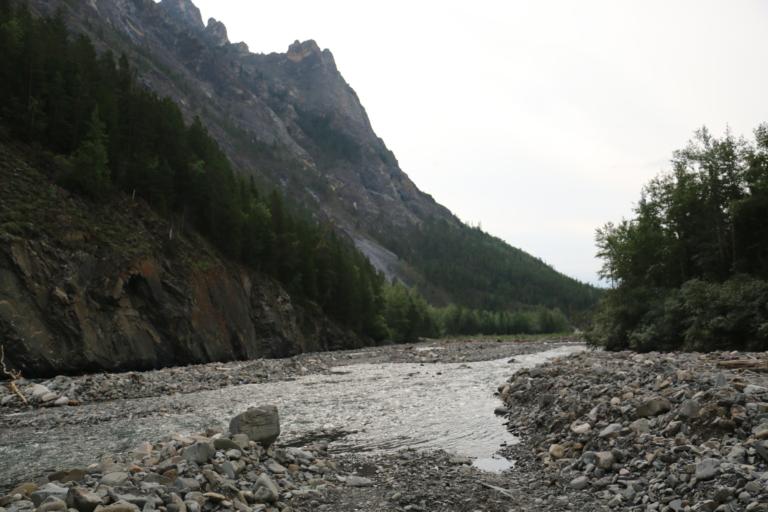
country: RU
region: Respublika Buryatiya
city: Novyy Uoyan
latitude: 56.2620
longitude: 111.4717
